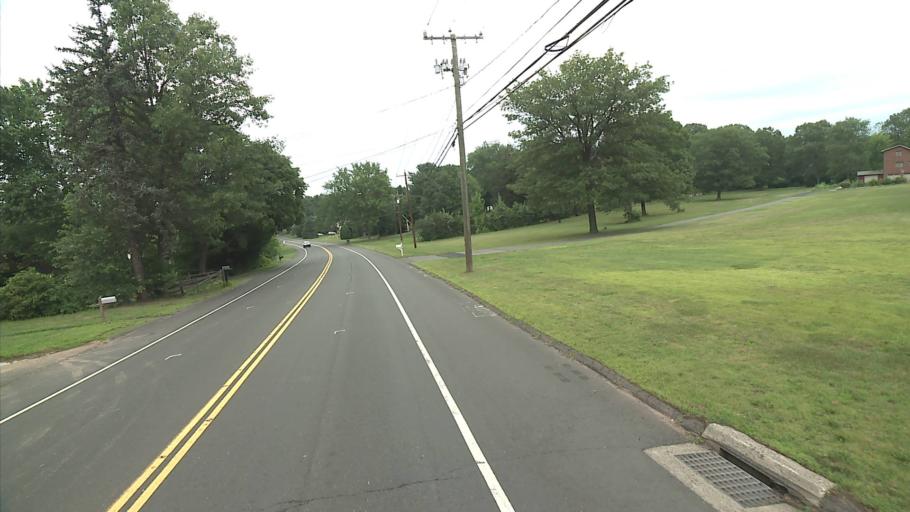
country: US
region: Connecticut
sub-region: Middlesex County
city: Cromwell
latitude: 41.6335
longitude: -72.6492
